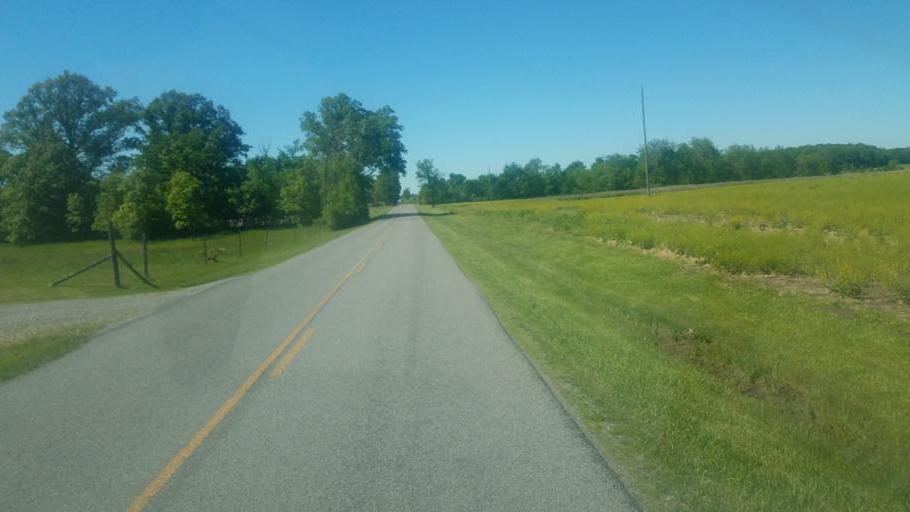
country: US
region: Ohio
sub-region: Logan County
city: Northwood
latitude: 40.4514
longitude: -83.7194
